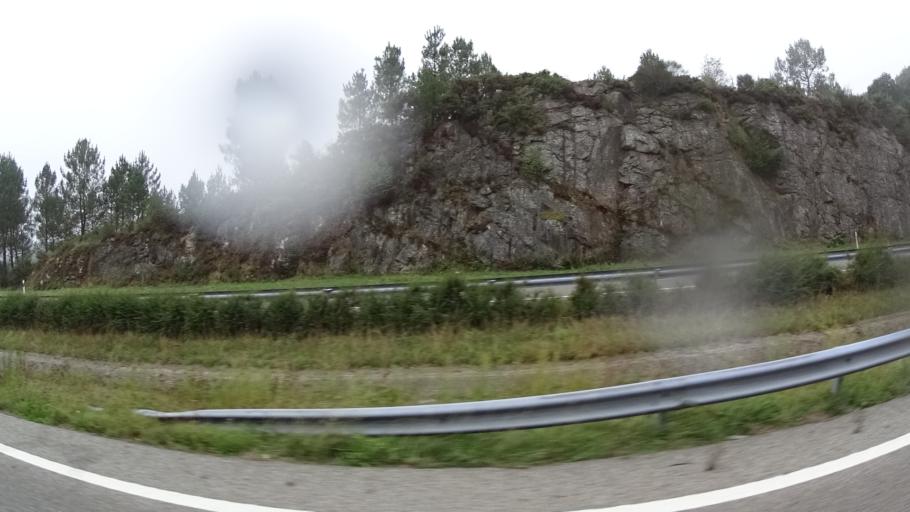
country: ES
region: Galicia
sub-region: Provincia de Lugo
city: Guitiriz
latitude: 43.1772
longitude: -7.8018
